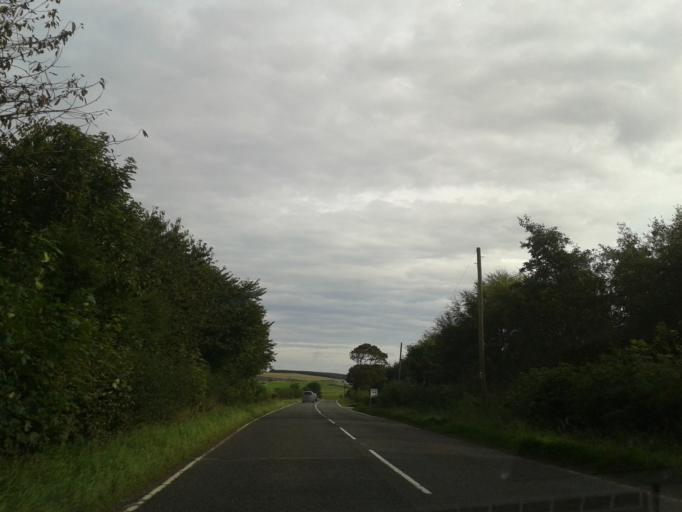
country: GB
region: Scotland
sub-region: Moray
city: Cullen
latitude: 57.6782
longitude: -2.7641
